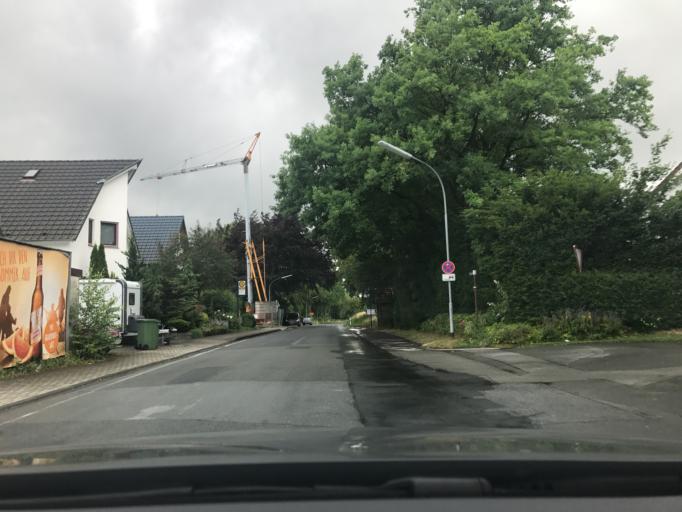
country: DE
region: North Rhine-Westphalia
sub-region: Regierungsbezirk Arnsberg
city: Mohnesee
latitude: 51.5283
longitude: 8.1663
